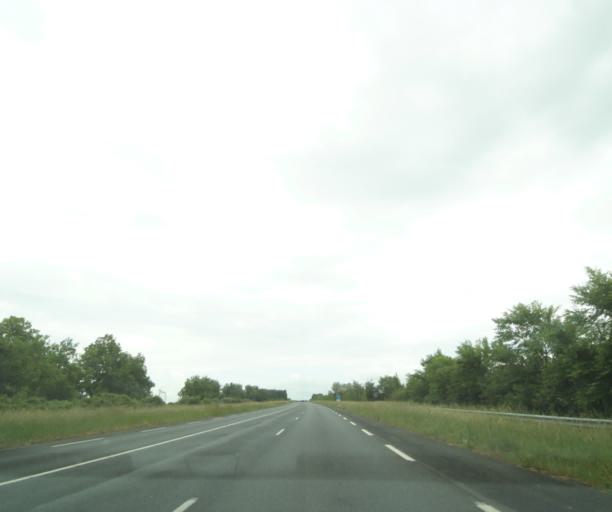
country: FR
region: Poitou-Charentes
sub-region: Departement des Deux-Sevres
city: Saint-Varent
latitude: 46.8530
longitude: -0.2087
